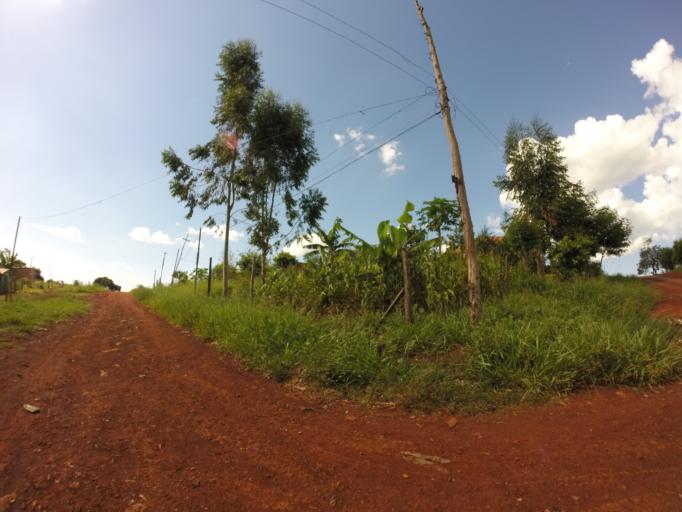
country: PY
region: Alto Parana
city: Ciudad del Este
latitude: -25.3777
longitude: -54.6614
